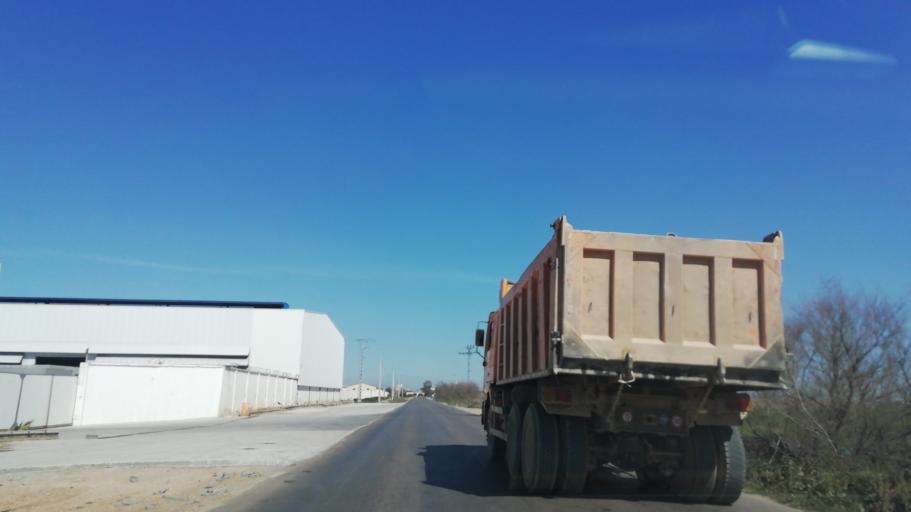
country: DZ
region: Oran
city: Es Senia
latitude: 35.5097
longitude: -0.5913
